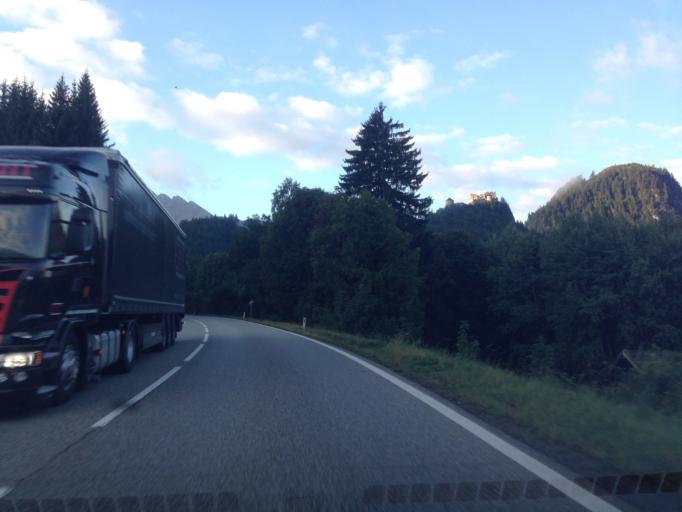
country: AT
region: Tyrol
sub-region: Politischer Bezirk Reutte
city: Breitenwang
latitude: 47.4724
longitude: 10.7256
